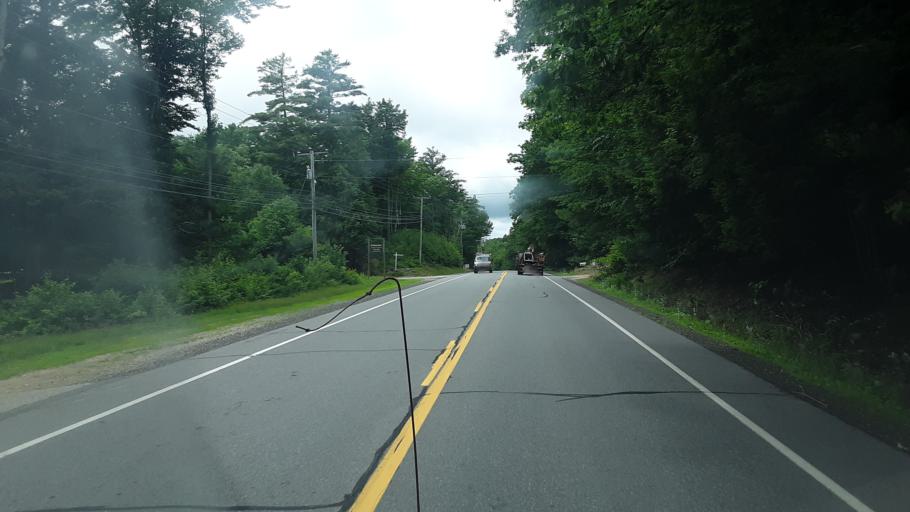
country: US
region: New Hampshire
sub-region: Rockingham County
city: Northwood
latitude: 43.1812
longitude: -71.1123
